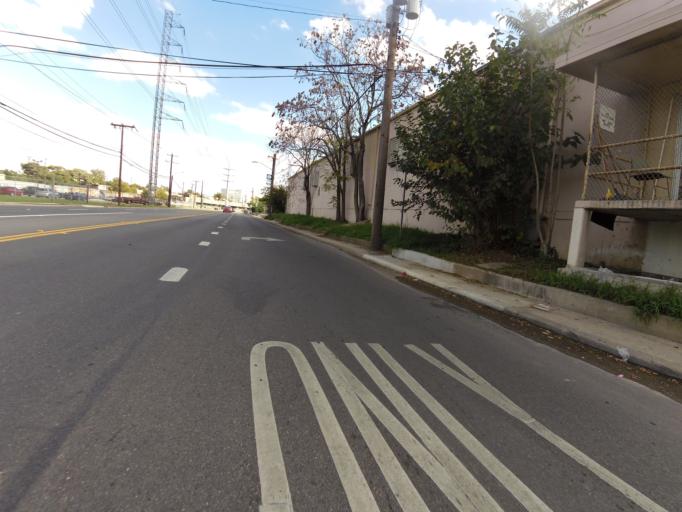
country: US
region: Texas
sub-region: Bexar County
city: San Antonio
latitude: 29.4103
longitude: -98.4984
